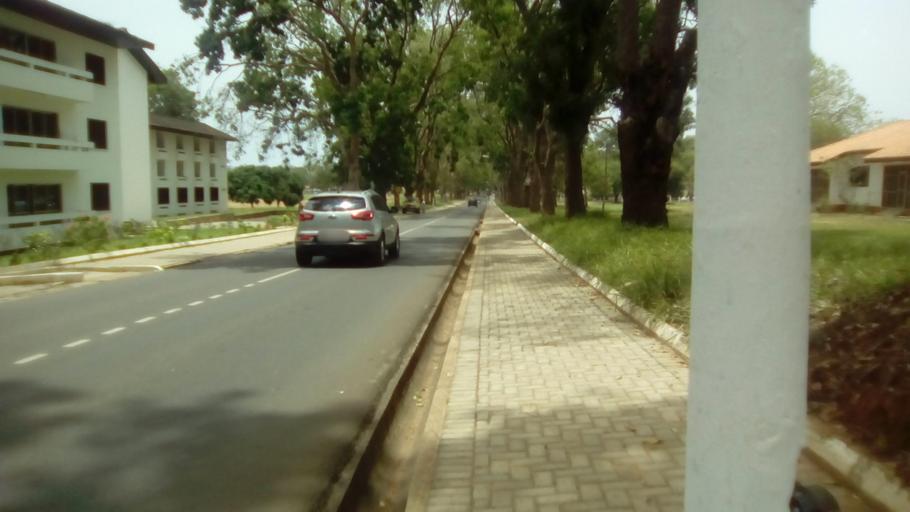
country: GH
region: Greater Accra
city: Medina Estates
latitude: 5.6476
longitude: -0.1891
